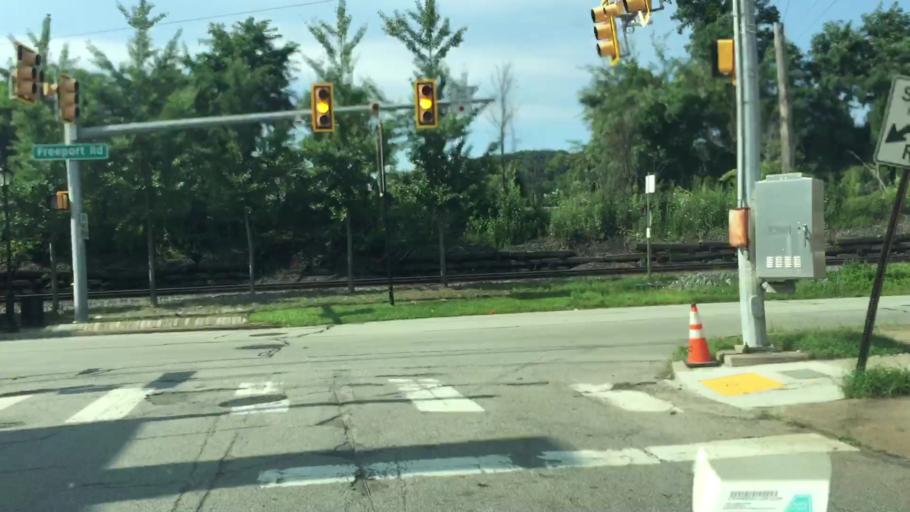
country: US
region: Pennsylvania
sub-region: Allegheny County
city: Aspinwall
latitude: 40.4908
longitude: -79.9074
